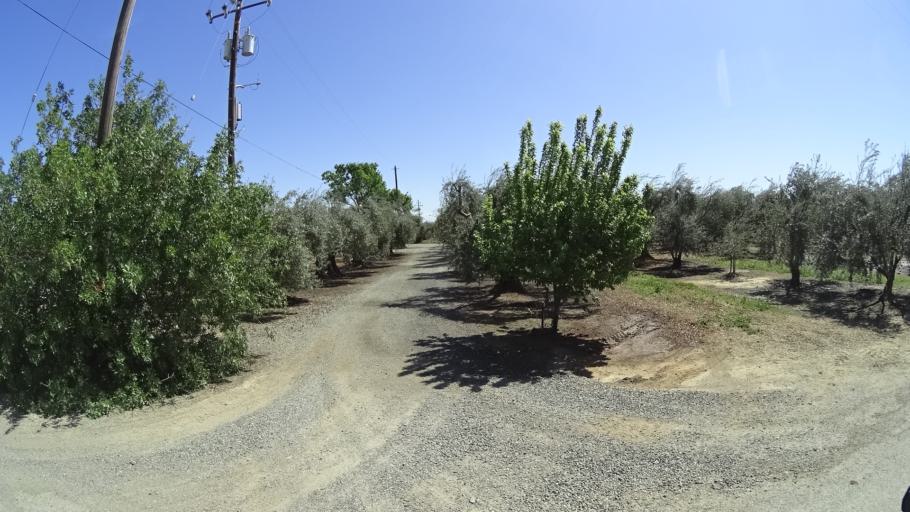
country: US
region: California
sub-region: Glenn County
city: Orland
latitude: 39.7036
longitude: -122.1641
